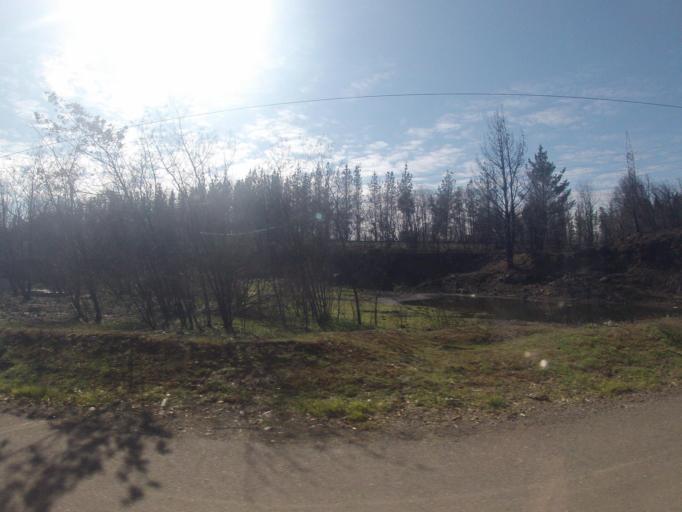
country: CL
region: Araucania
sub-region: Provincia de Malleco
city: Victoria
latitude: -38.1490
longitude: -72.3066
